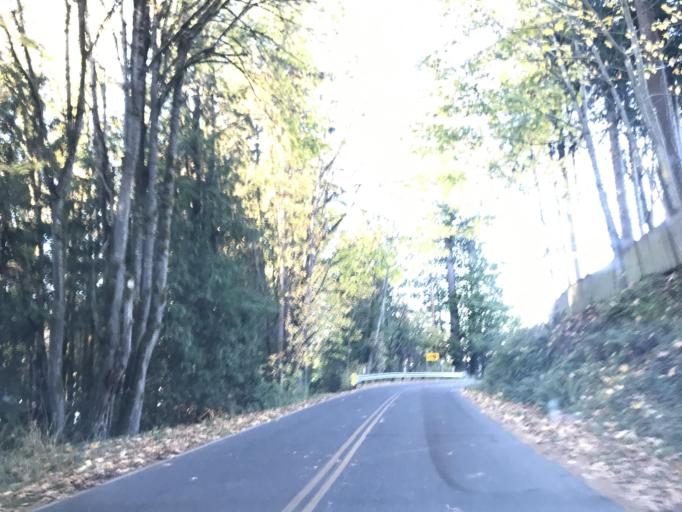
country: US
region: Washington
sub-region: Whatcom County
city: Geneva
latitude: 48.7483
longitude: -122.4074
